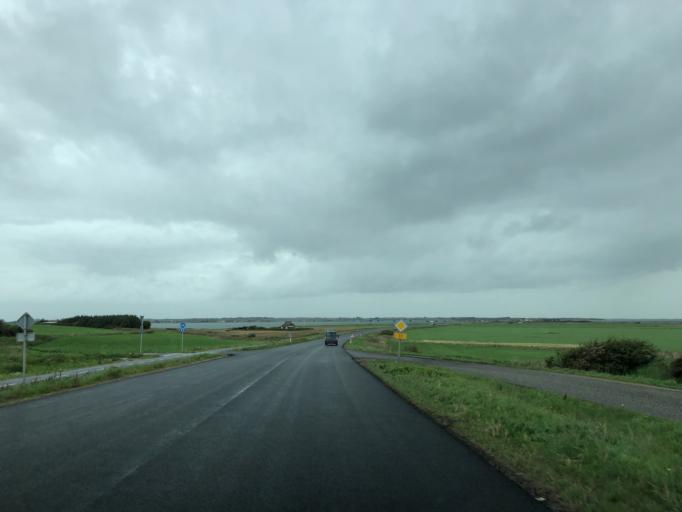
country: DK
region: Central Jutland
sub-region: Struer Kommune
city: Struer
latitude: 56.5575
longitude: 8.5573
